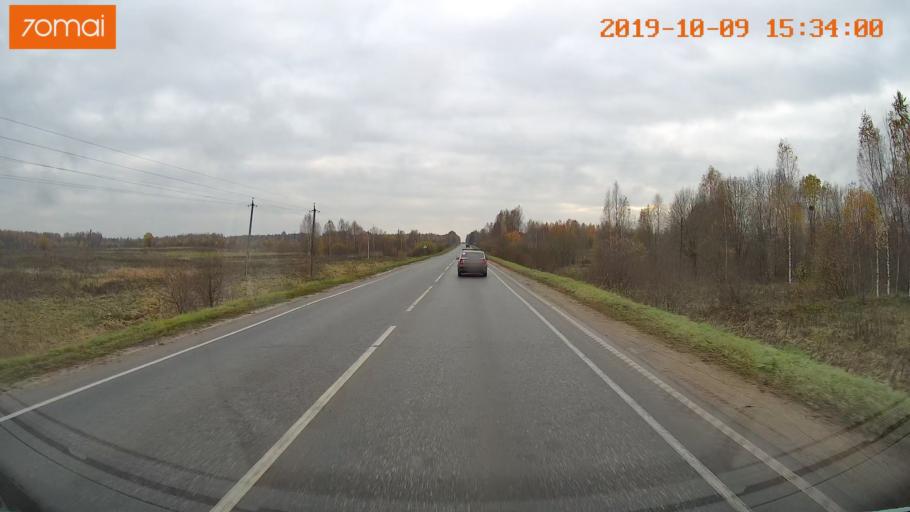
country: RU
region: Kostroma
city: Oktyabr'skiy
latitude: 57.9450
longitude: 41.2532
